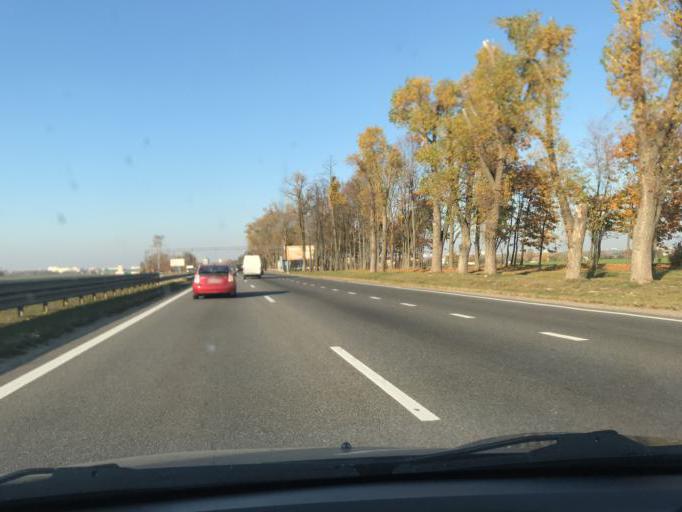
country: BY
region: Minsk
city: Yubilyeyny
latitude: 53.7996
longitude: 27.5295
